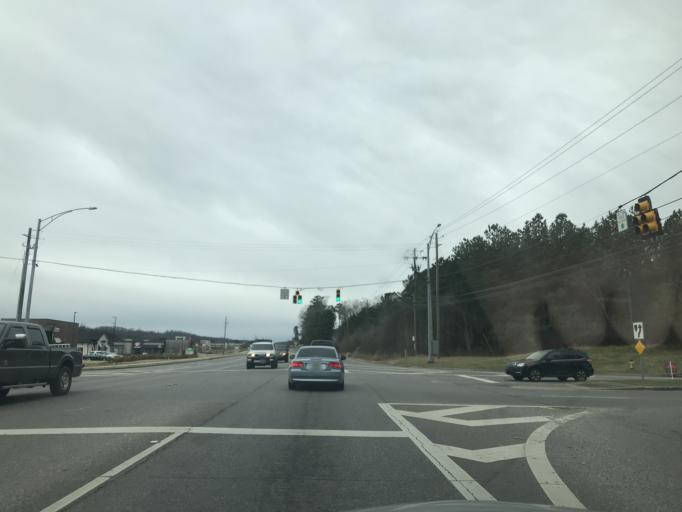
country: US
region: Alabama
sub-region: Shelby County
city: Brook Highland
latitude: 33.4261
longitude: -86.6685
